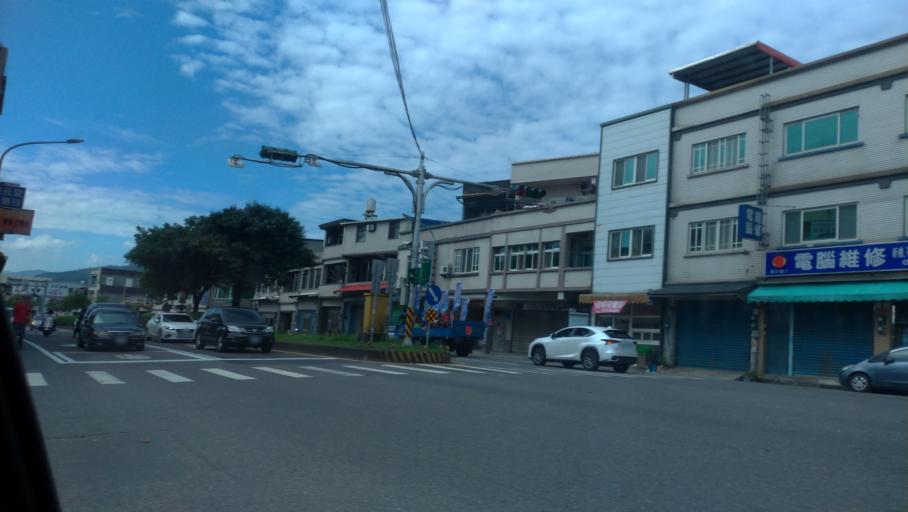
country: TW
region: Taiwan
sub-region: Yilan
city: Yilan
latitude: 24.8453
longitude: 121.8076
